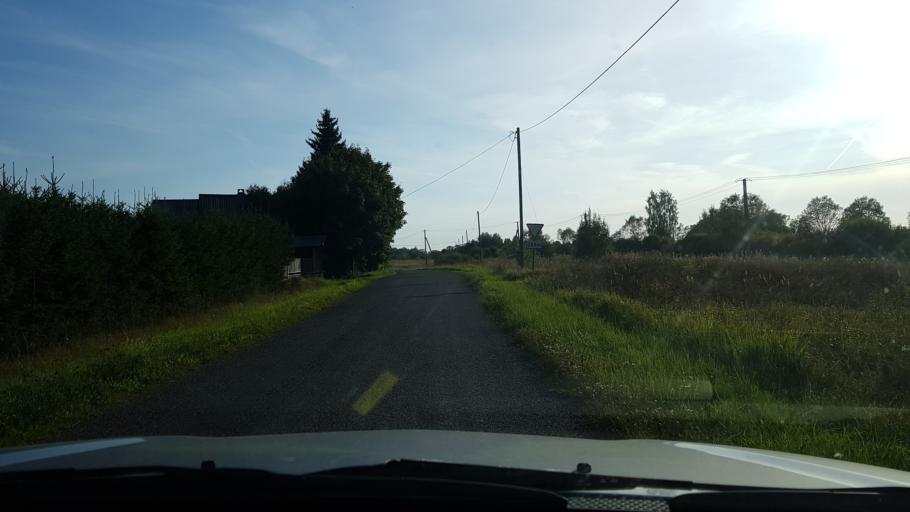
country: EE
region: Ida-Virumaa
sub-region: Narva-Joesuu linn
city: Narva-Joesuu
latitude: 59.3505
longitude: 28.0298
